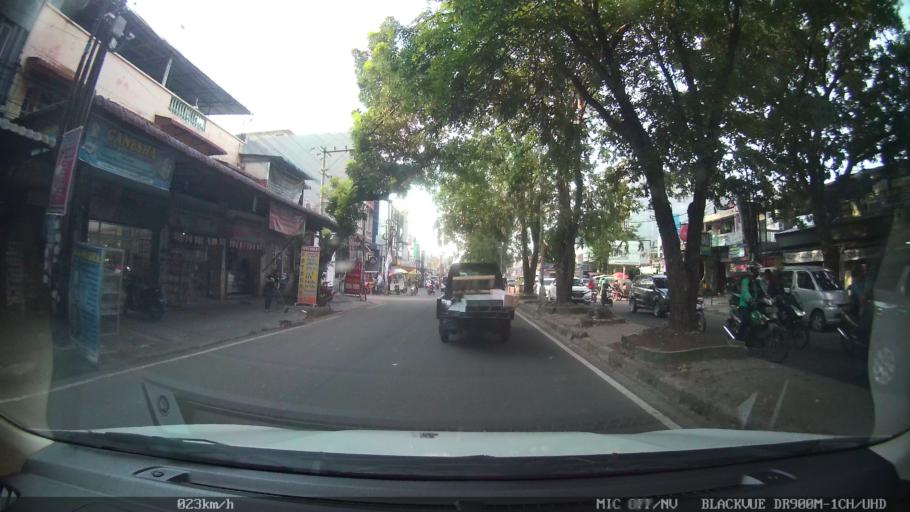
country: ID
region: North Sumatra
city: Medan
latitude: 3.5726
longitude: 98.6426
